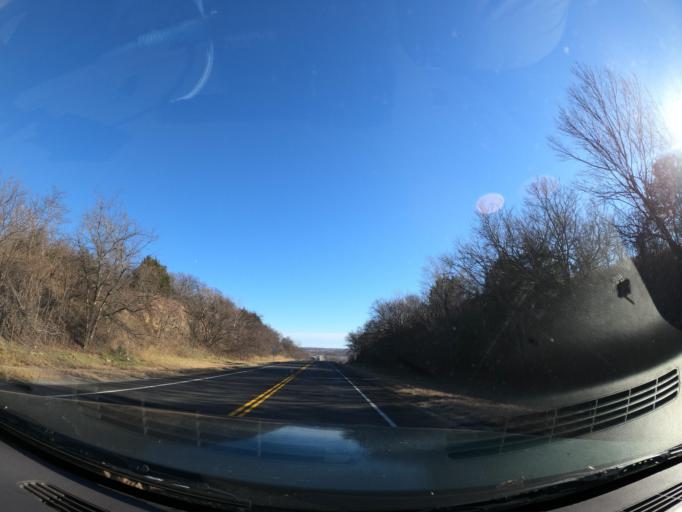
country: US
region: Oklahoma
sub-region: McIntosh County
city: Eufaula
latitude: 35.2522
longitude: -95.5732
